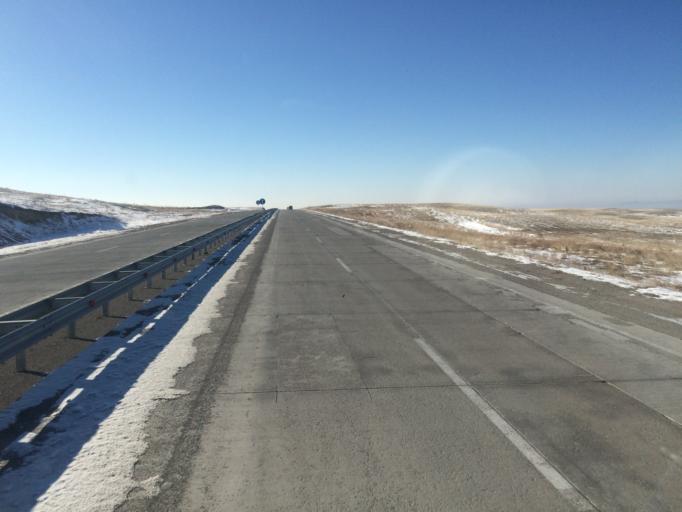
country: KZ
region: Zhambyl
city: Georgiyevka
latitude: 43.3743
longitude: 74.7486
